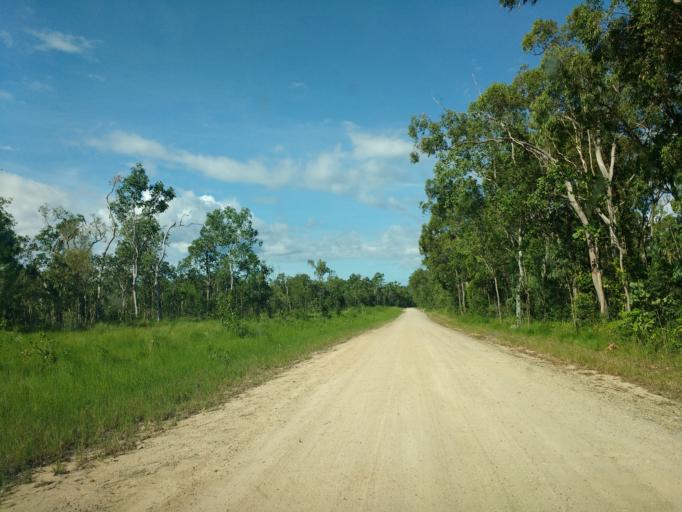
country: AU
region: Queensland
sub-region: Hinchinbrook
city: Ingham
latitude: -18.3275
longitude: 146.0463
